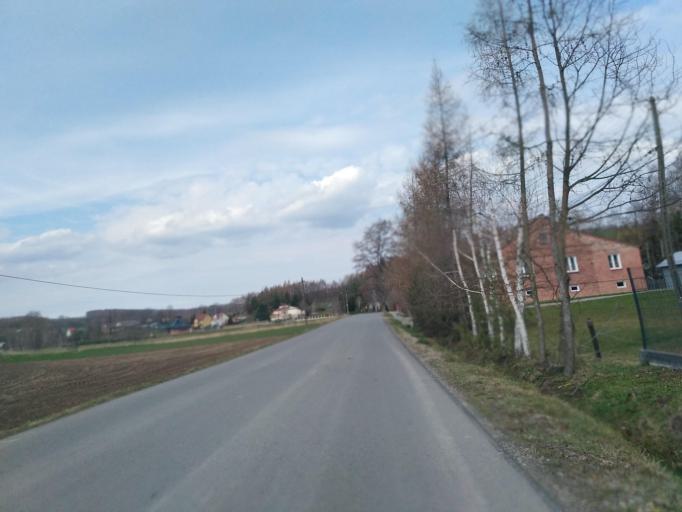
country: PL
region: Subcarpathian Voivodeship
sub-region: Powiat ropczycko-sedziszowski
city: Iwierzyce
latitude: 50.0334
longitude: 21.7564
